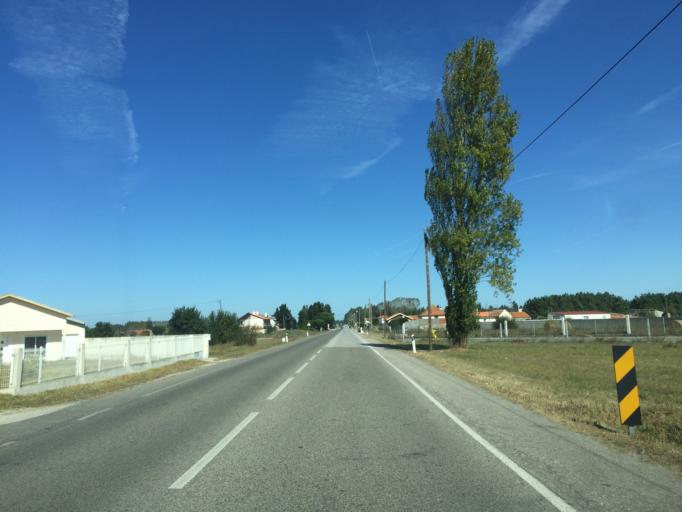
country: PT
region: Coimbra
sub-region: Figueira da Foz
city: Alhadas
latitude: 40.2338
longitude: -8.7976
